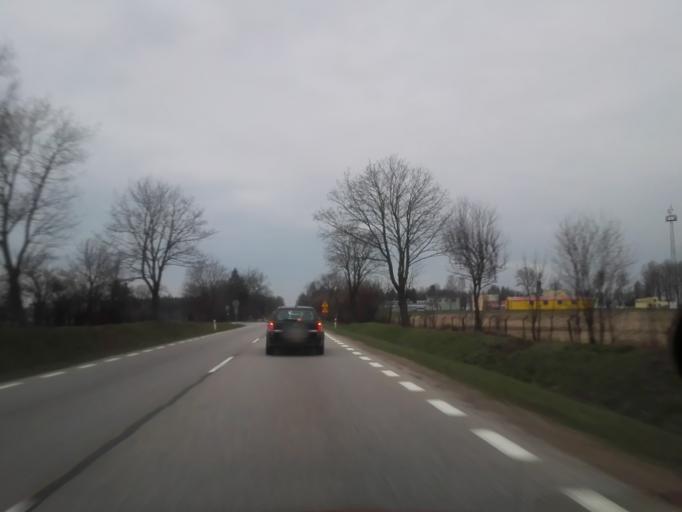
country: PL
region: Podlasie
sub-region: Powiat lomzynski
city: Piatnica
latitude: 53.2143
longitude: 22.1055
